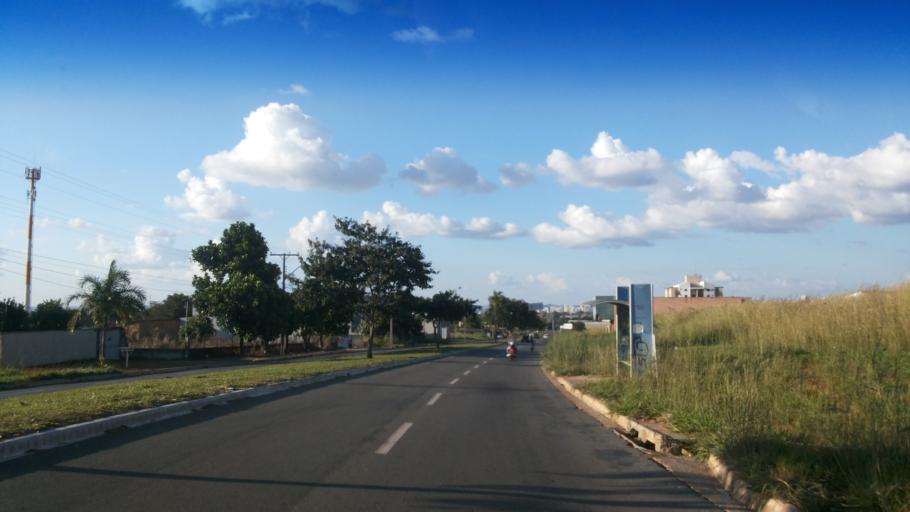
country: BR
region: Goias
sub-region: Goiania
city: Goiania
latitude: -16.7473
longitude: -49.3188
